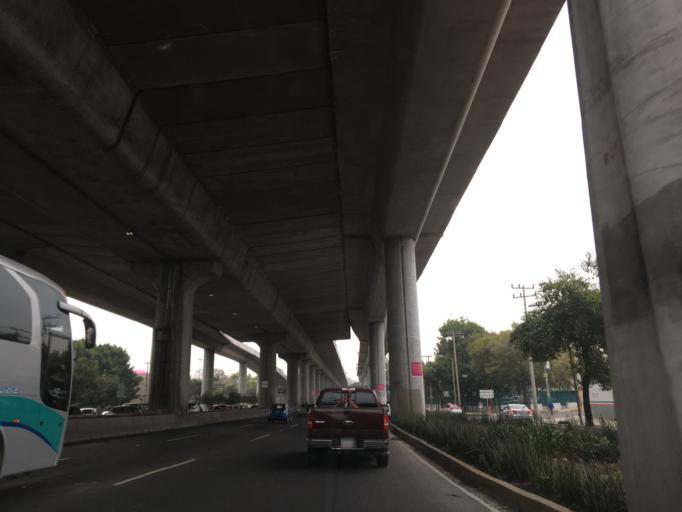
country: MX
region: Mexico City
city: Tlalpan
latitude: 19.2933
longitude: -99.1541
